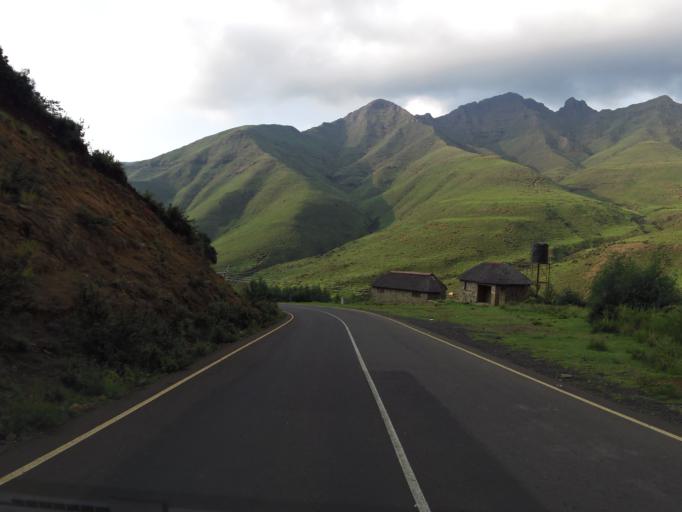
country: LS
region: Butha-Buthe
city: Butha-Buthe
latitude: -29.0532
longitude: 28.3453
